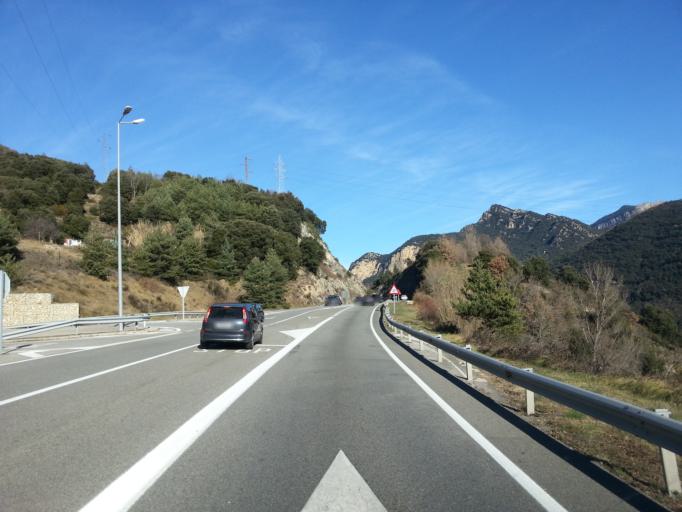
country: ES
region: Catalonia
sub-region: Provincia de Barcelona
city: Berga
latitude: 42.1552
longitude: 1.8579
